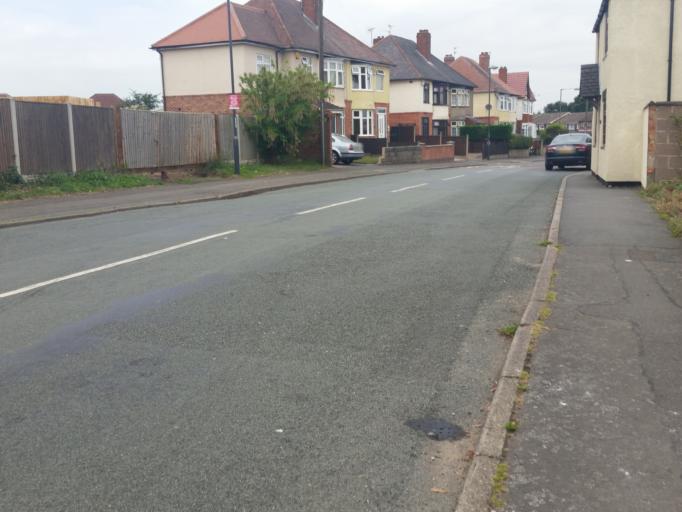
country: GB
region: England
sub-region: Derbyshire
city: Borrowash
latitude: 52.8979
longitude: -1.4218
